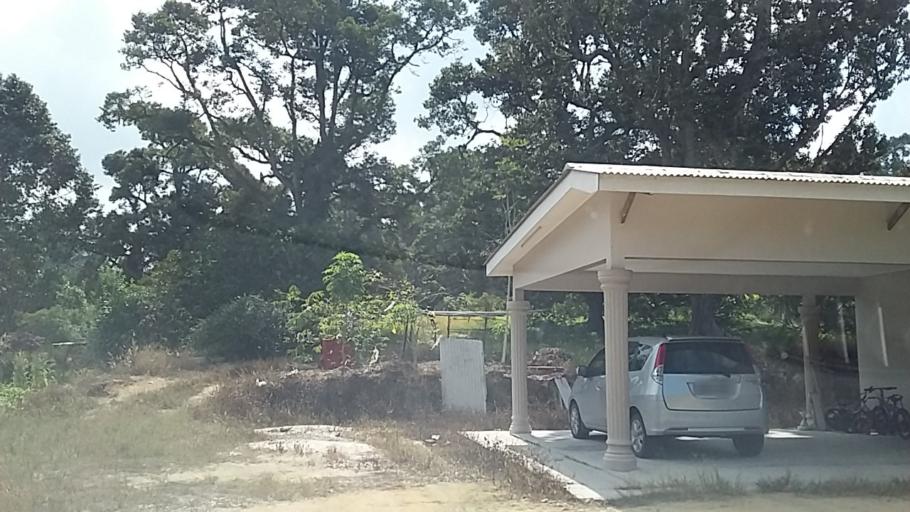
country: MY
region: Johor
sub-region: Daerah Batu Pahat
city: Batu Pahat
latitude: 1.7891
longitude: 102.8991
